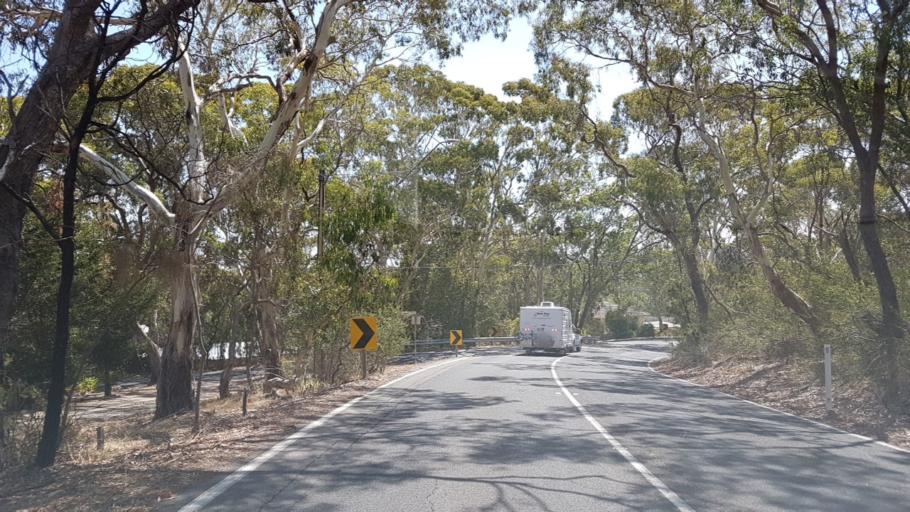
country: AU
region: South Australia
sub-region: Mitcham
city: Blackwood
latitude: -35.0146
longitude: 138.6342
